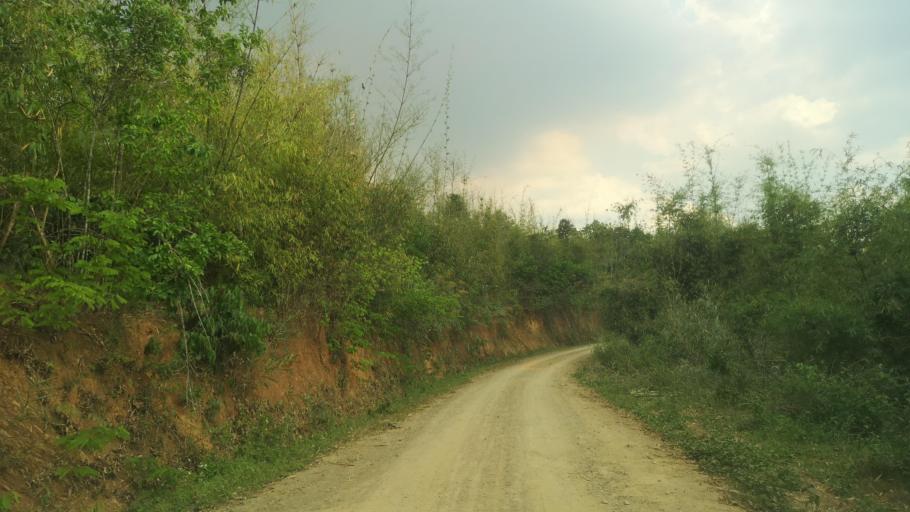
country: LA
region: Loungnamtha
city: Muang Nale
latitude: 20.3302
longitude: 101.3373
